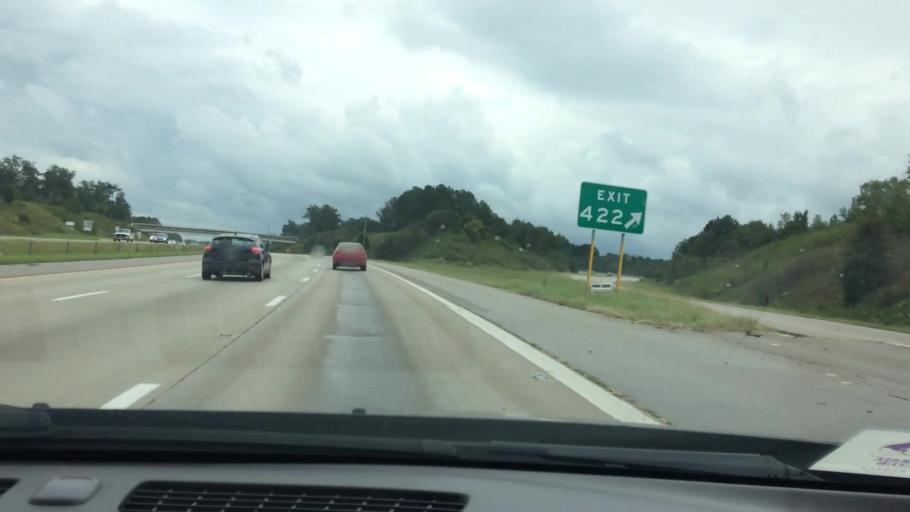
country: US
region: North Carolina
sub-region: Wake County
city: Knightdale
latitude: 35.7687
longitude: -78.5256
